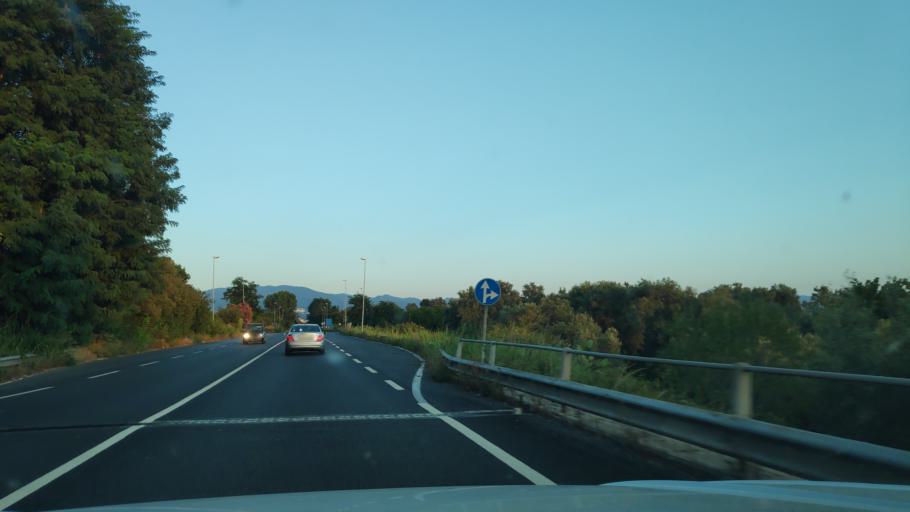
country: IT
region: Calabria
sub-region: Provincia di Reggio Calabria
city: Melicucco
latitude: 38.4304
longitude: 16.0538
